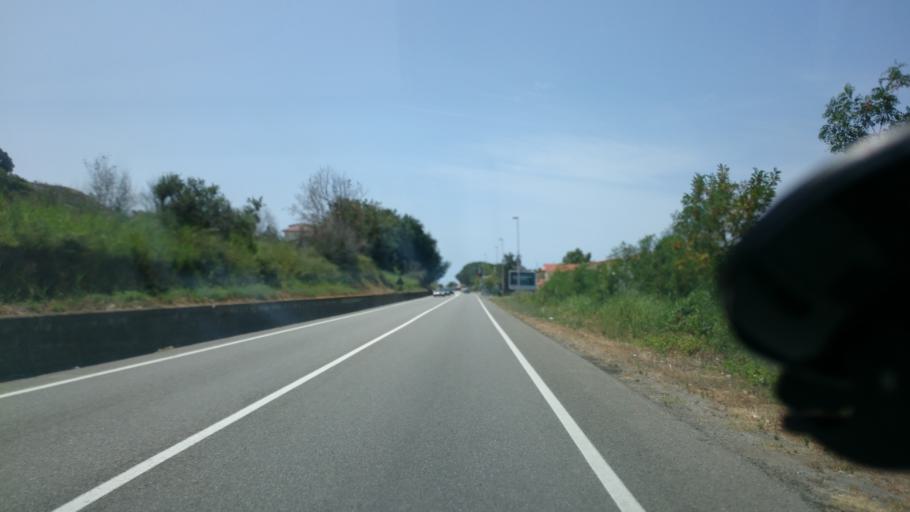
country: IT
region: Calabria
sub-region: Provincia di Cosenza
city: Cittadella del Capo
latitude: 39.5823
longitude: 15.8697
